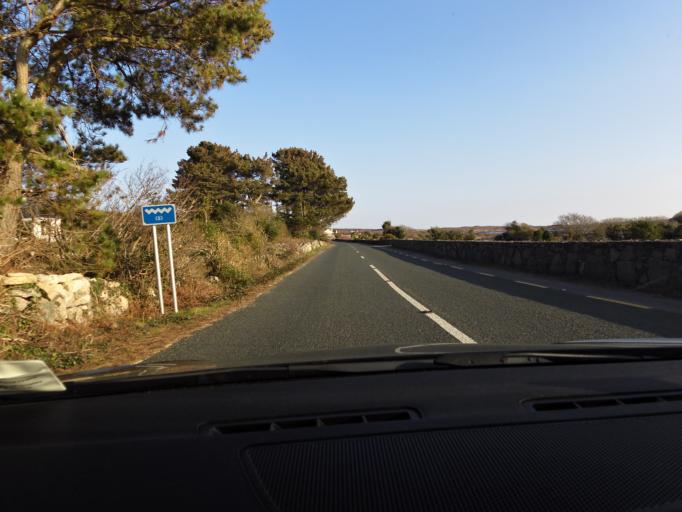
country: IE
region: Connaught
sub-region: County Galway
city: Oughterard
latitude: 53.3846
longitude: -9.6062
